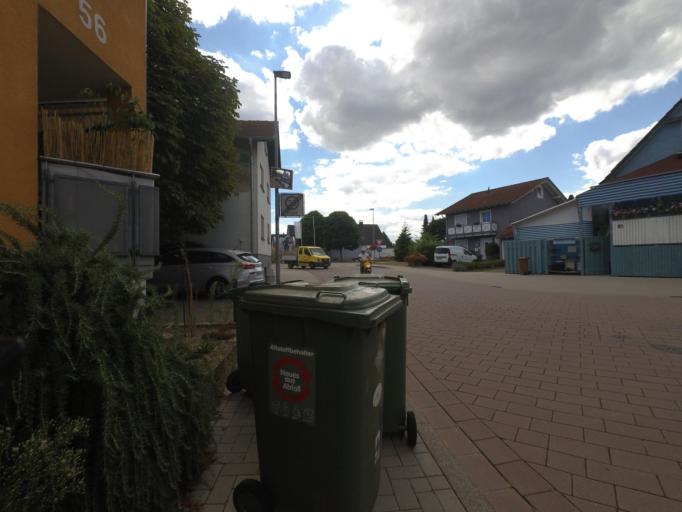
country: DE
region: Baden-Wuerttemberg
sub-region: Karlsruhe Region
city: Sinzheim
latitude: 48.7739
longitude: 8.1691
